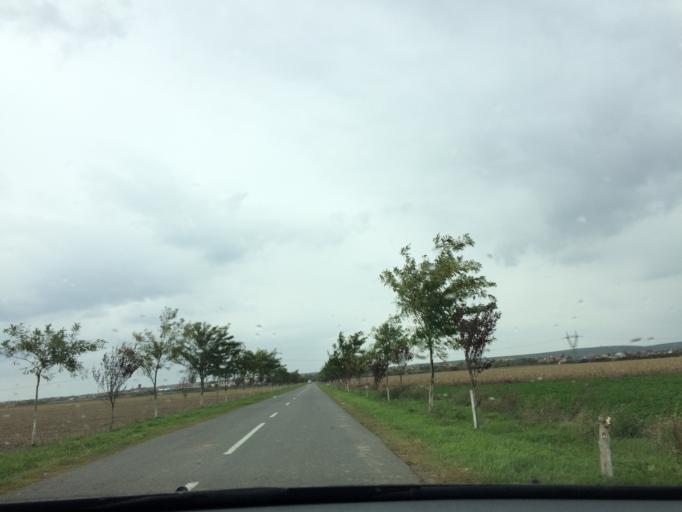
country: RO
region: Timis
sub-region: Oras Recas
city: Recas
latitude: 45.7853
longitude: 21.5150
